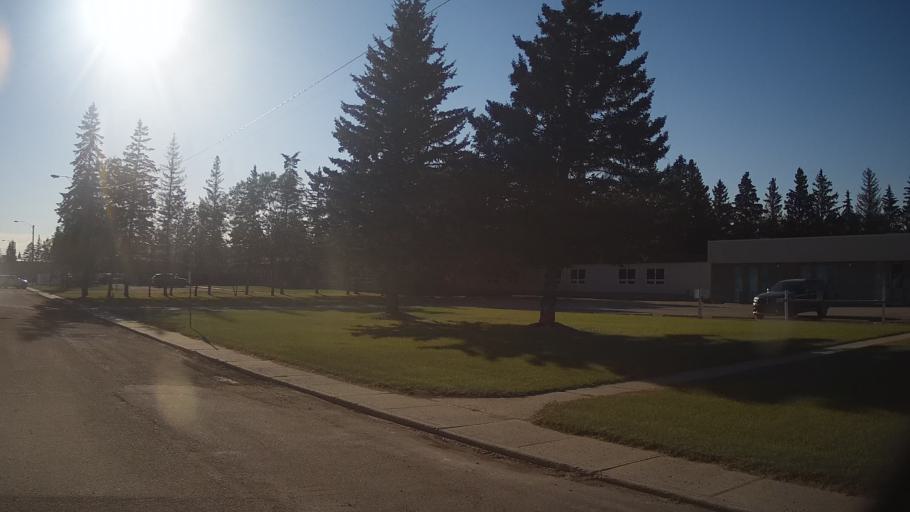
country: CA
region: Saskatchewan
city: Lanigan
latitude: 51.8509
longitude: -105.0238
